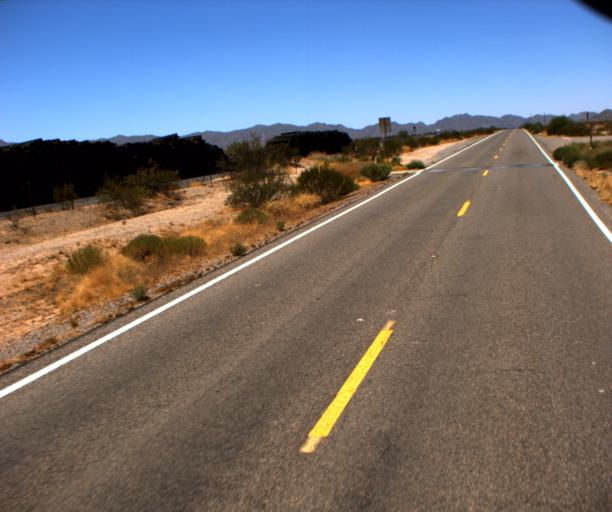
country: US
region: Arizona
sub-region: Pinal County
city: Maricopa
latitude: 33.0227
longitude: -112.3766
